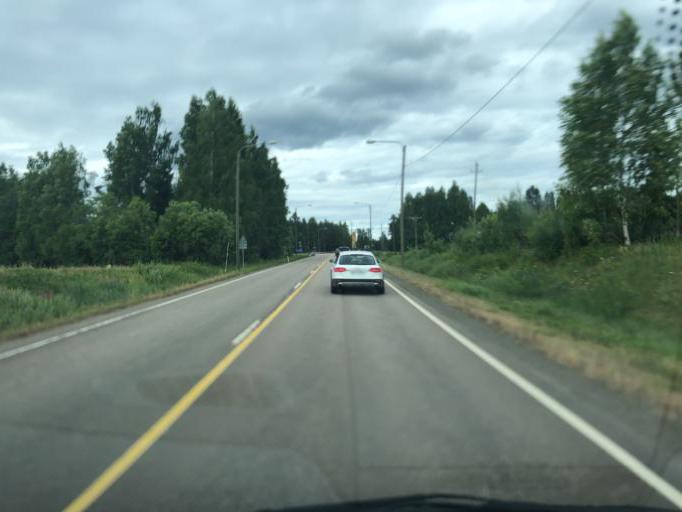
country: FI
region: Southern Savonia
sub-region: Mikkeli
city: Maentyharju
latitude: 61.0873
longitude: 27.0658
